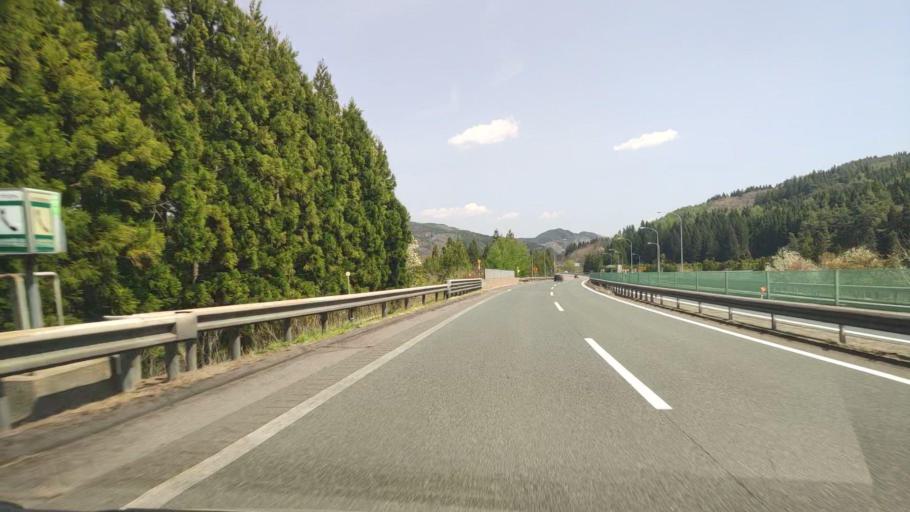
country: JP
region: Iwate
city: Ichinohe
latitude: 40.1917
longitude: 141.1741
